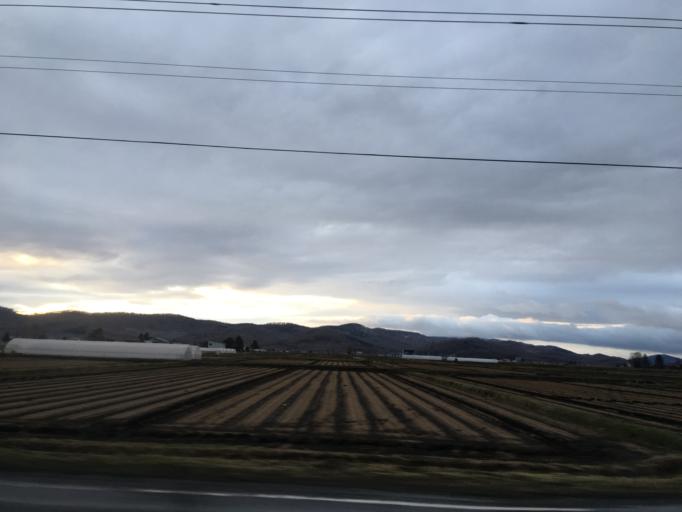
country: JP
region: Hokkaido
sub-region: Asahikawa-shi
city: Asahikawa
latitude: 43.8805
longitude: 142.4912
